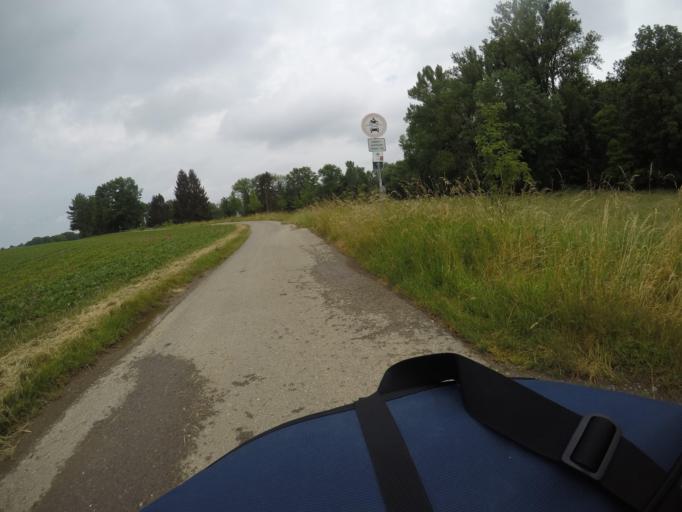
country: DE
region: Baden-Wuerttemberg
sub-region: Regierungsbezirk Stuttgart
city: Ditzingen
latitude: 48.8376
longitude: 9.0584
